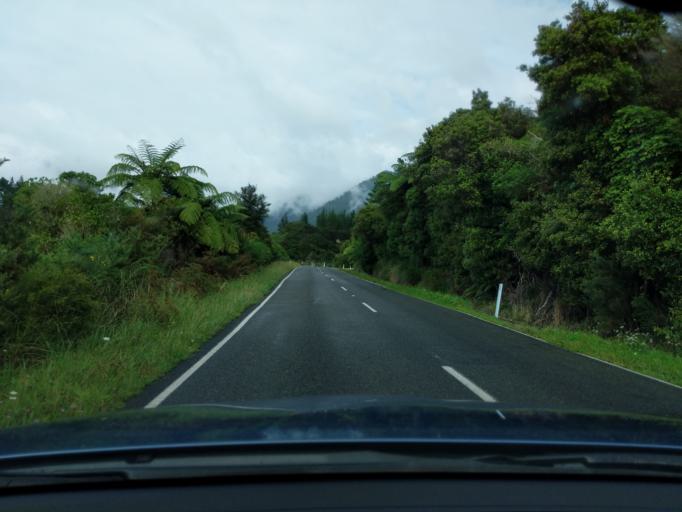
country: NZ
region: Tasman
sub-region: Tasman District
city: Takaka
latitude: -40.6393
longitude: 172.6679
